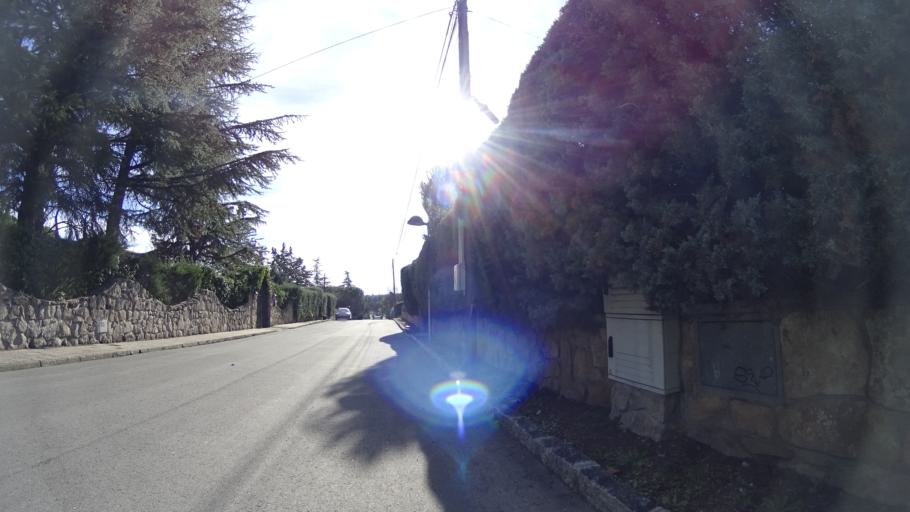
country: ES
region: Madrid
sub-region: Provincia de Madrid
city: Galapagar
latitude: 40.5800
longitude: -4.0226
